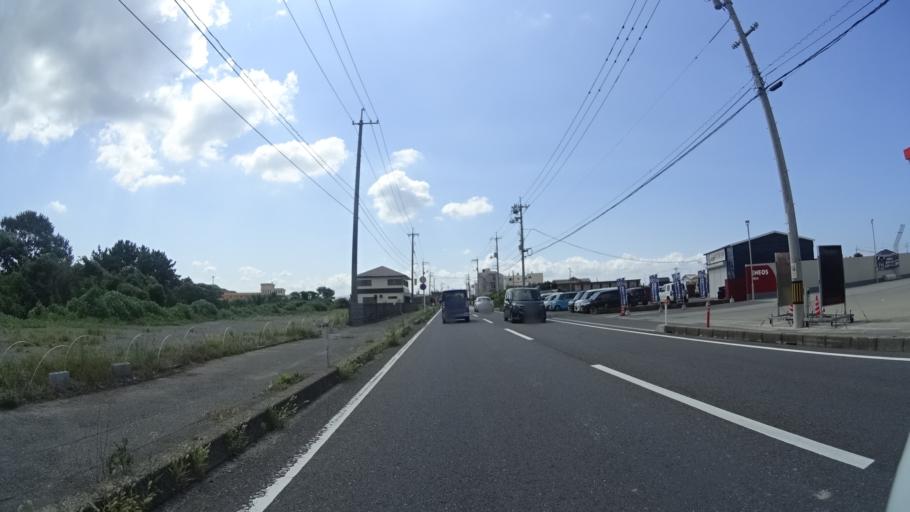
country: JP
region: Yamaguchi
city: Shimonoseki
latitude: 34.0371
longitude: 130.9138
